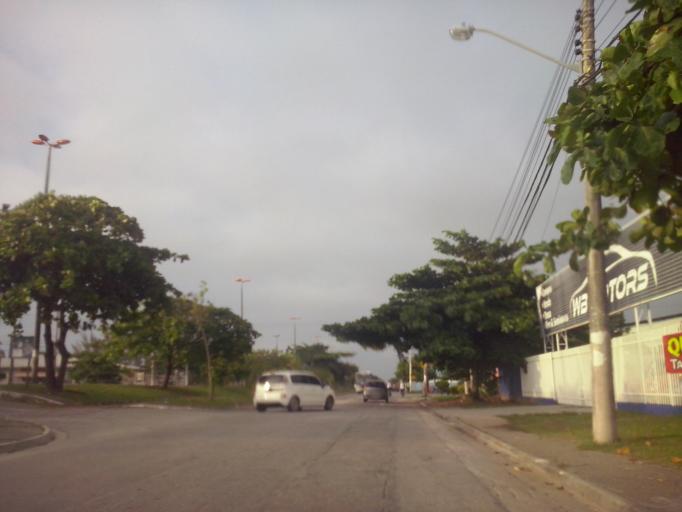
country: BR
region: Rio de Janeiro
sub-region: Rio Das Ostras
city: Rio das Ostras
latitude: -22.5479
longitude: -41.9743
